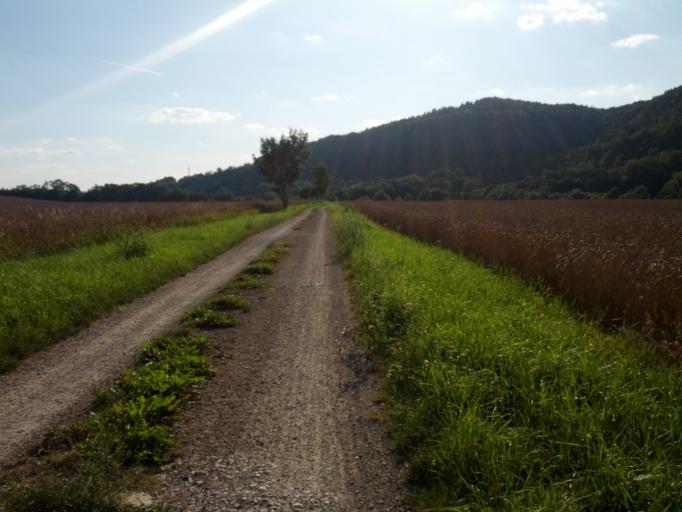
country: DE
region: Thuringia
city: Creuzburg
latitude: 51.0590
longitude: 10.2610
